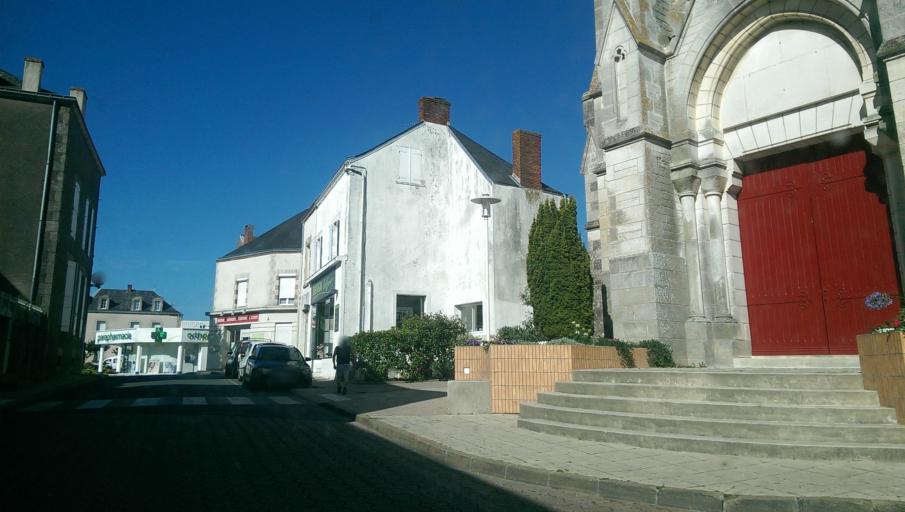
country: FR
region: Pays de la Loire
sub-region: Departement de la Vendee
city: Aizenay
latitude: 46.7398
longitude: -1.6094
